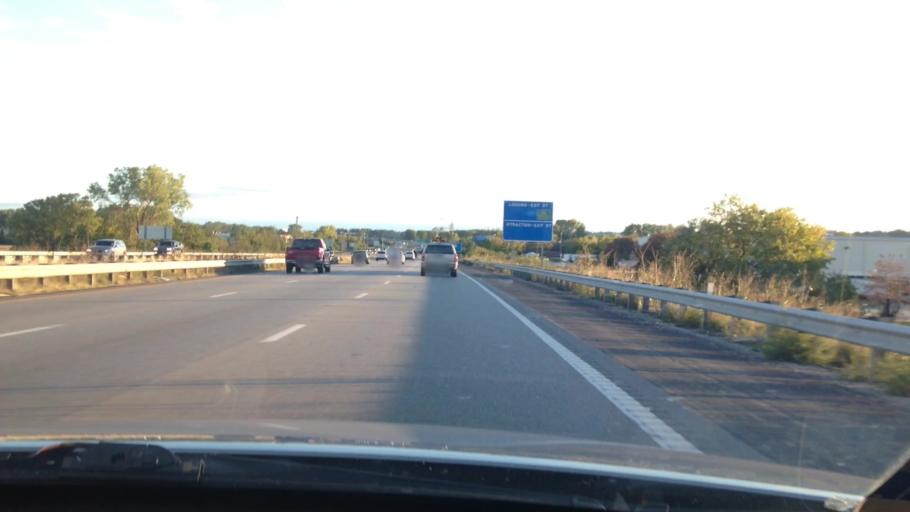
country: US
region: Missouri
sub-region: Clay County
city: Claycomo
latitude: 39.1433
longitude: -94.4987
